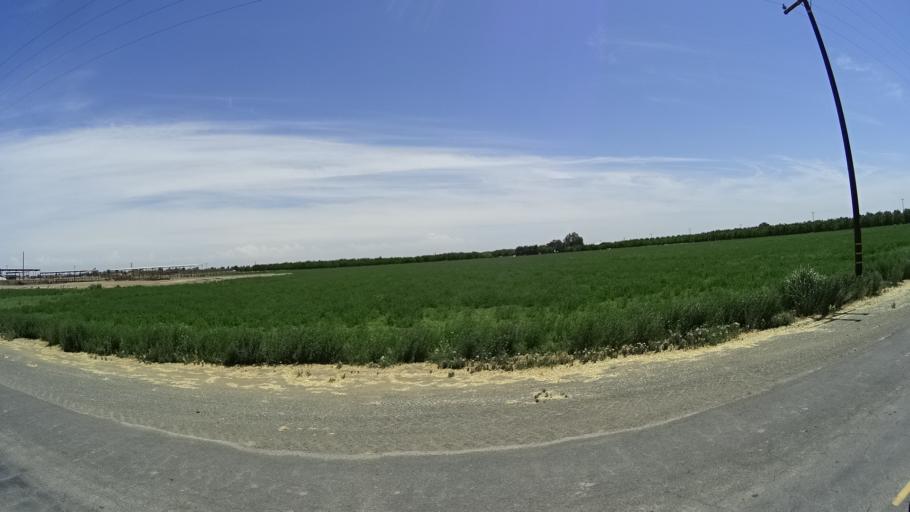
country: US
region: California
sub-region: Kings County
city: Armona
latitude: 36.3336
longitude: -119.7270
